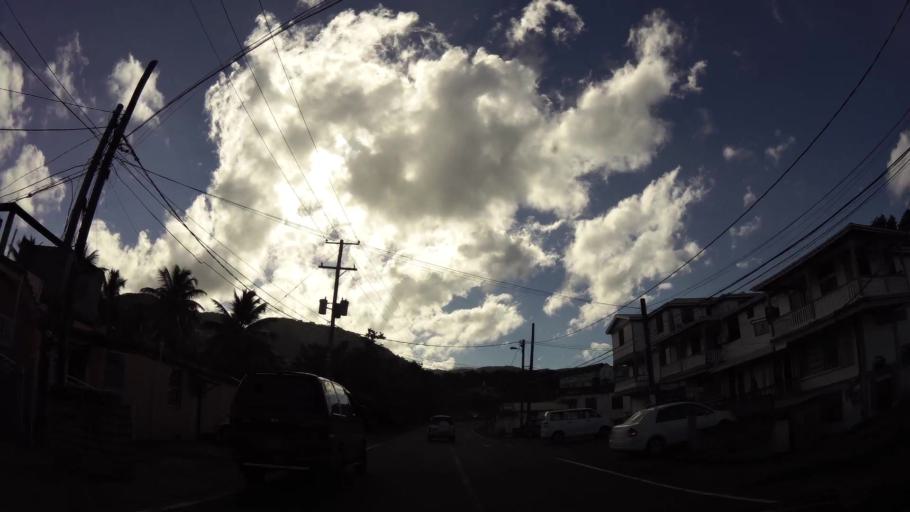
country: DM
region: Saint John
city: Portsmouth
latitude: 15.5638
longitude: -61.4544
